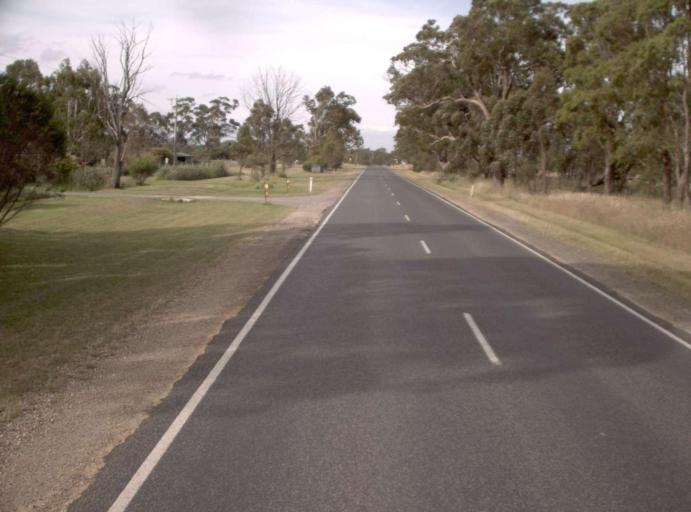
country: AU
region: Victoria
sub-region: Latrobe
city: Traralgon
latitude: -38.0682
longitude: 146.6165
